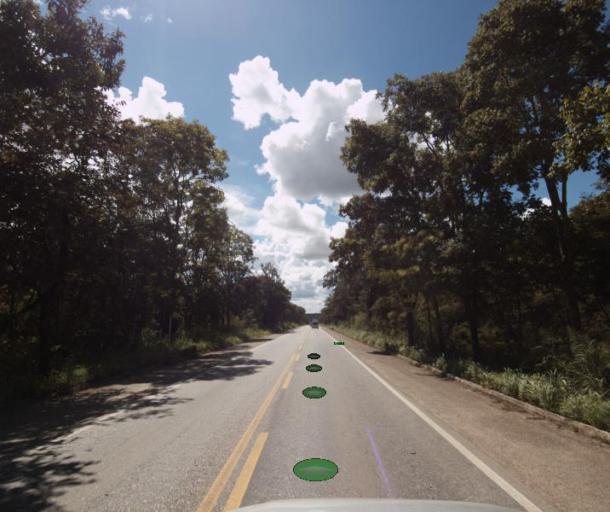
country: BR
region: Goias
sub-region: Porangatu
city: Porangatu
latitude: -13.6594
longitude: -49.0343
